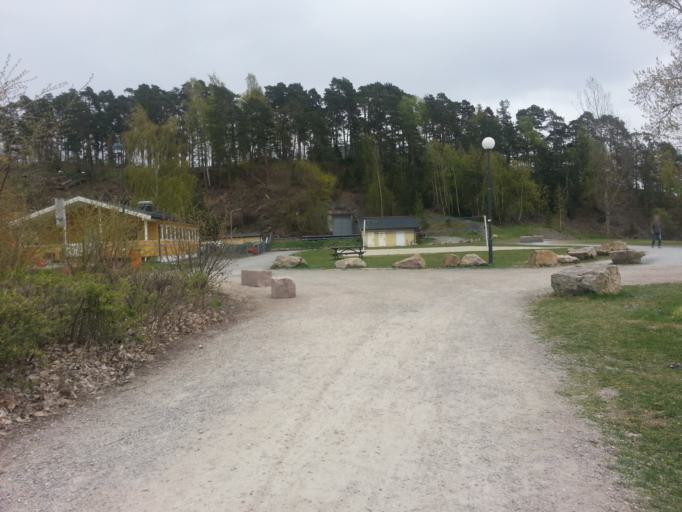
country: NO
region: Akershus
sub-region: Baerum
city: Lysaker
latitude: 59.9130
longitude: 10.6469
